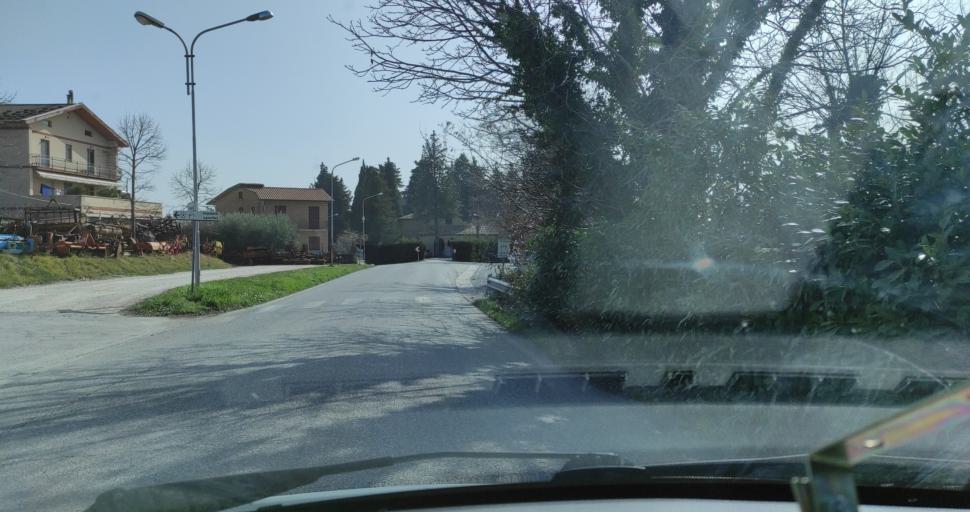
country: IT
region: The Marches
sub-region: Provincia di Macerata
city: Loro Piceno
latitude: 43.1630
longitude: 13.4222
